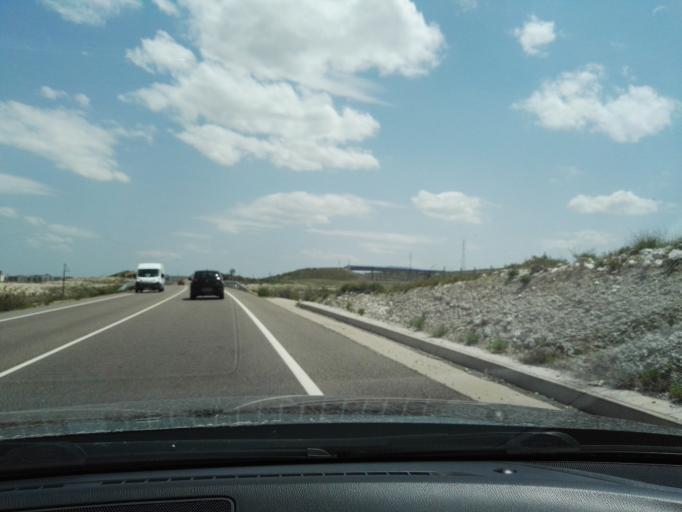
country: ES
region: Aragon
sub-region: Provincia de Zaragoza
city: Montecanal
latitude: 41.6220
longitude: -0.9799
